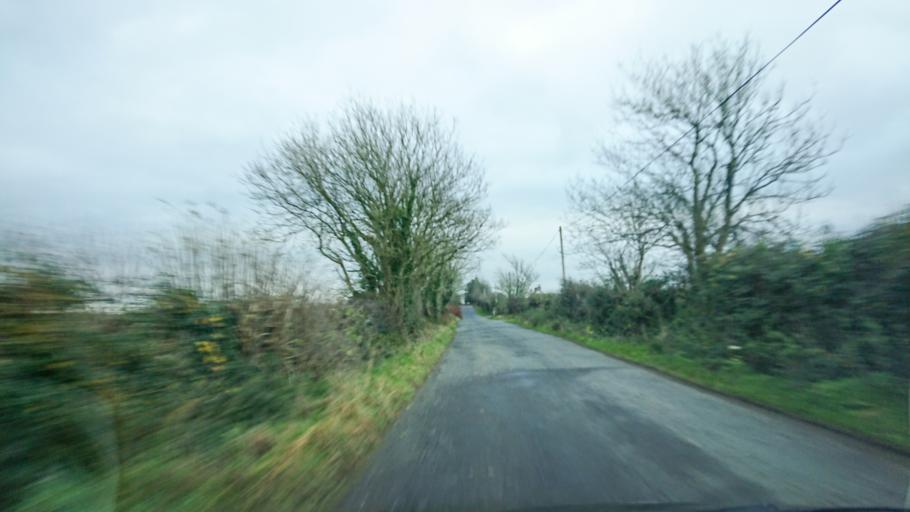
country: IE
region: Munster
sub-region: Waterford
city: Dunmore East
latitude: 52.2396
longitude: -6.9923
